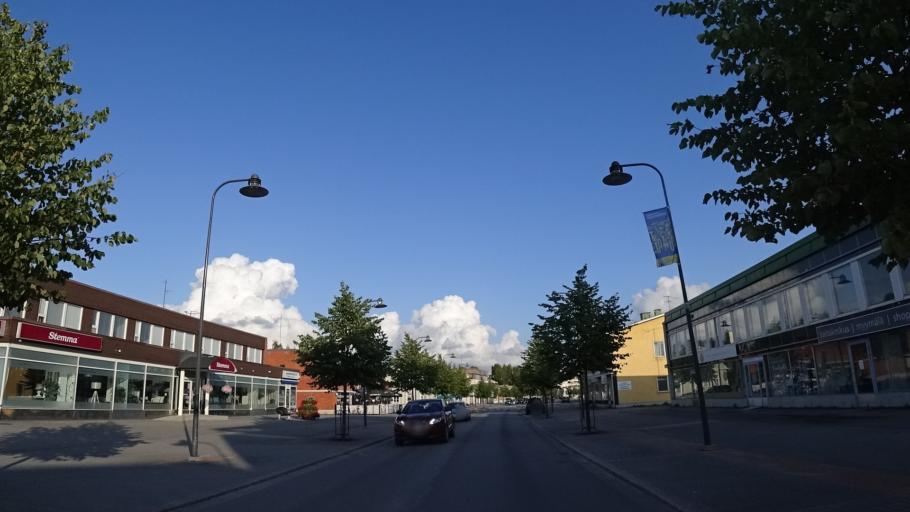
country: FI
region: North Karelia
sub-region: Pielisen Karjala
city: Lieksa
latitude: 63.3182
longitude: 30.0274
